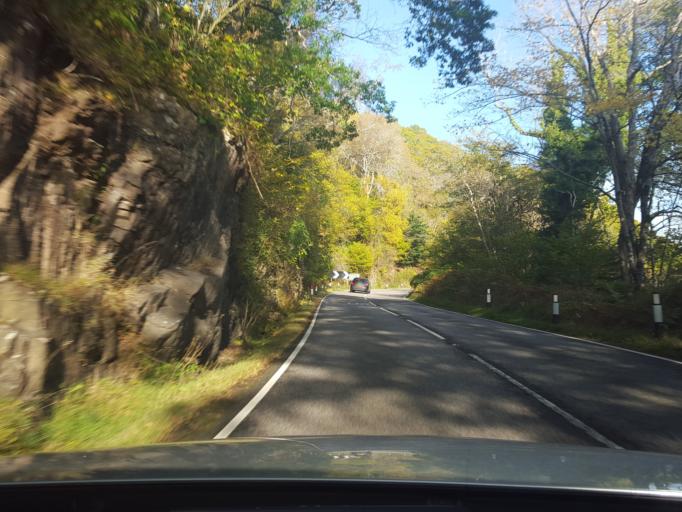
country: GB
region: Scotland
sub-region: Highland
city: Beauly
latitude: 57.2835
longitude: -4.4894
